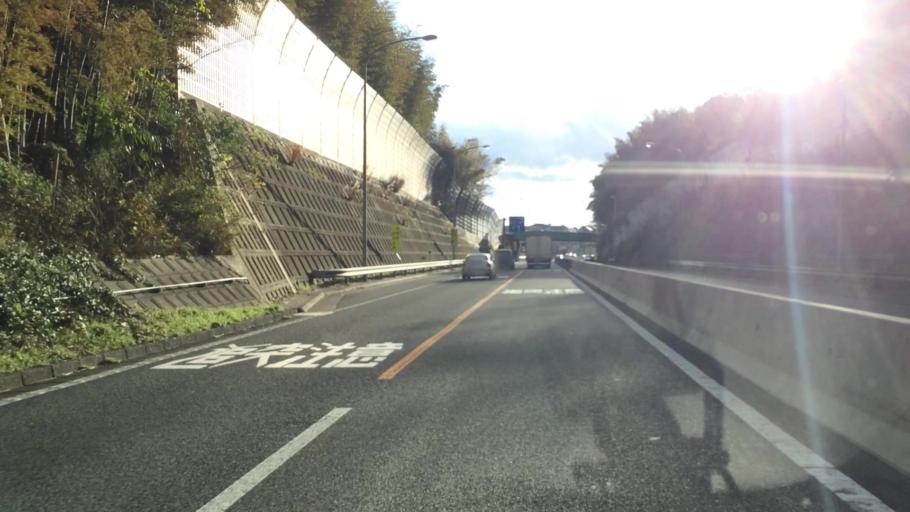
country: JP
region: Kanagawa
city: Fujisawa
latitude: 35.4150
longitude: 139.5357
